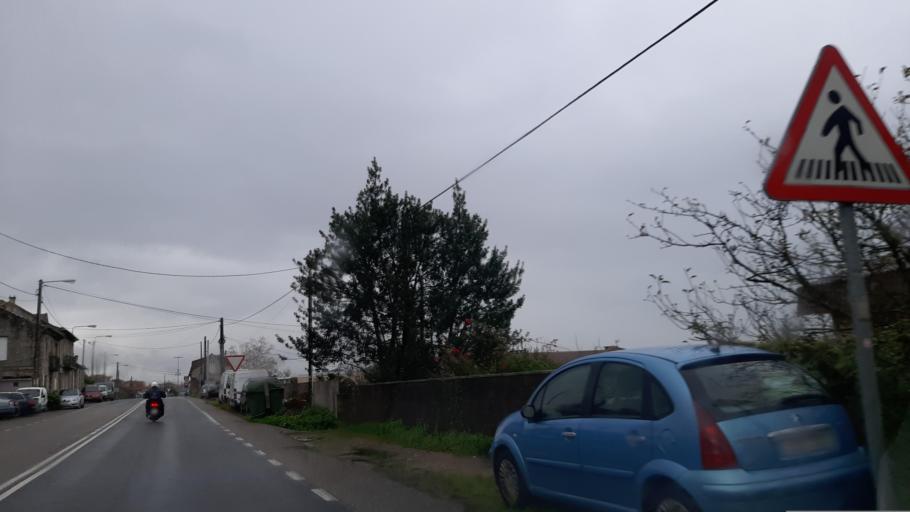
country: ES
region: Galicia
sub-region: Provincia de Pontevedra
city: Nigran
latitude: 42.1688
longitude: -8.8012
